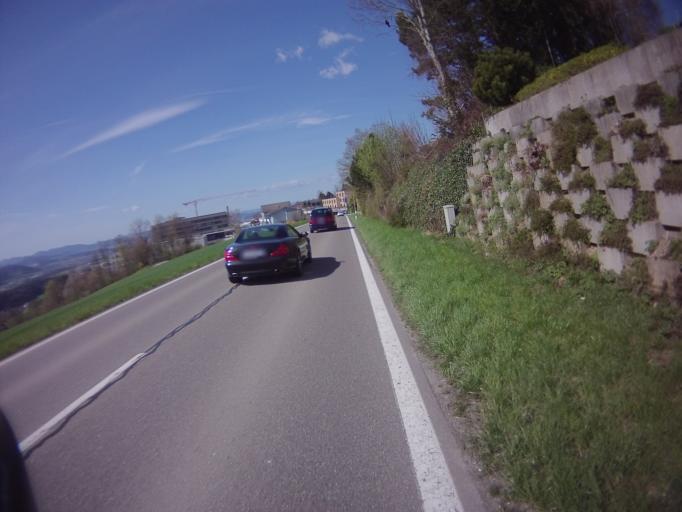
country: CH
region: Aargau
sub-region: Bezirk Baden
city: Kunten
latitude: 47.3854
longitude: 8.3471
